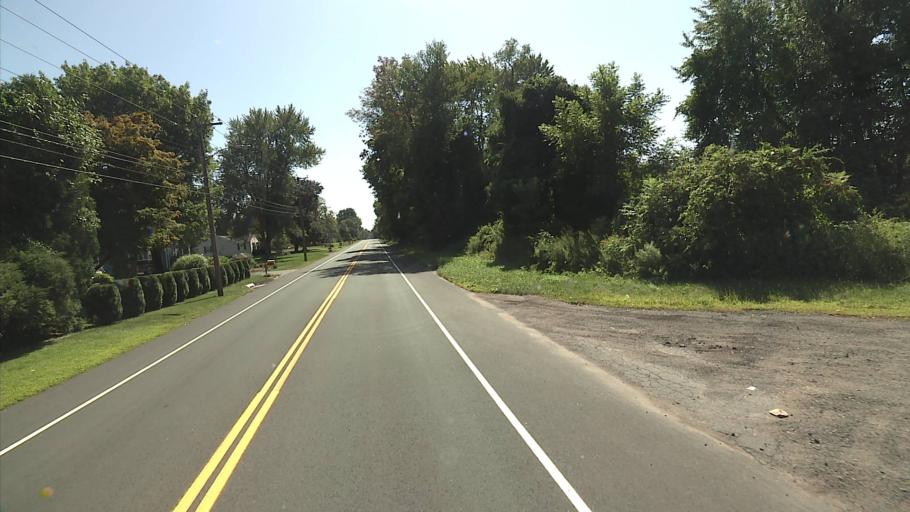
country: US
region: Connecticut
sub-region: Hartford County
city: Windsor Locks
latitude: 41.9013
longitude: -72.6255
